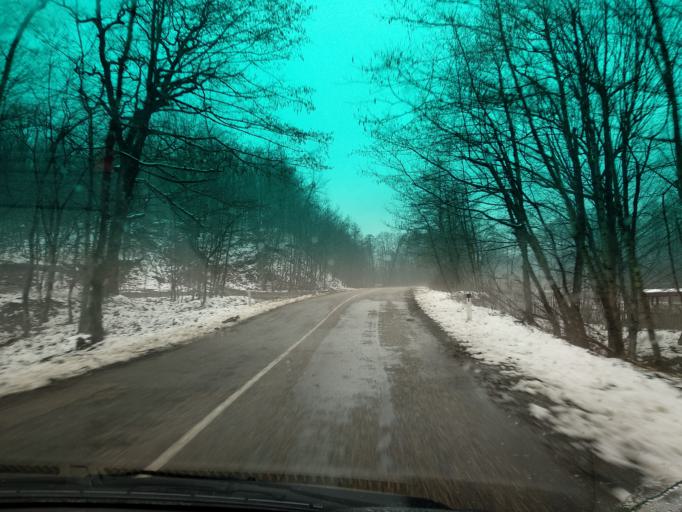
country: RU
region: Krasnodarskiy
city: Khadyzhensk
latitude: 44.2095
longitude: 39.4202
